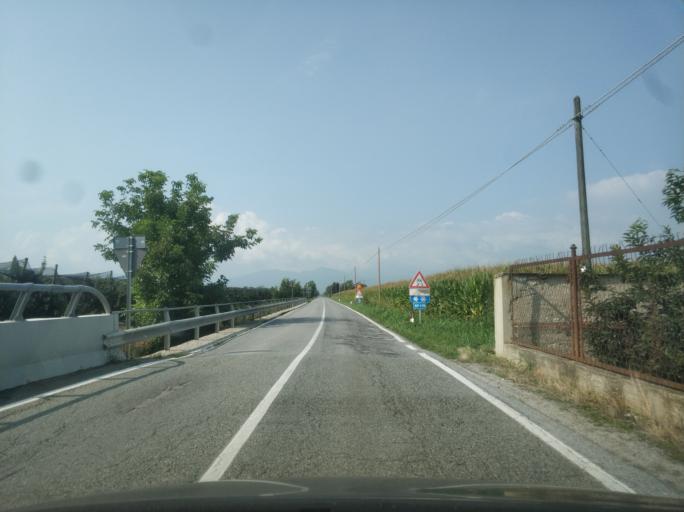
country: IT
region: Piedmont
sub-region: Provincia di Cuneo
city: Roata Rossi
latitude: 44.4707
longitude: 7.5102
